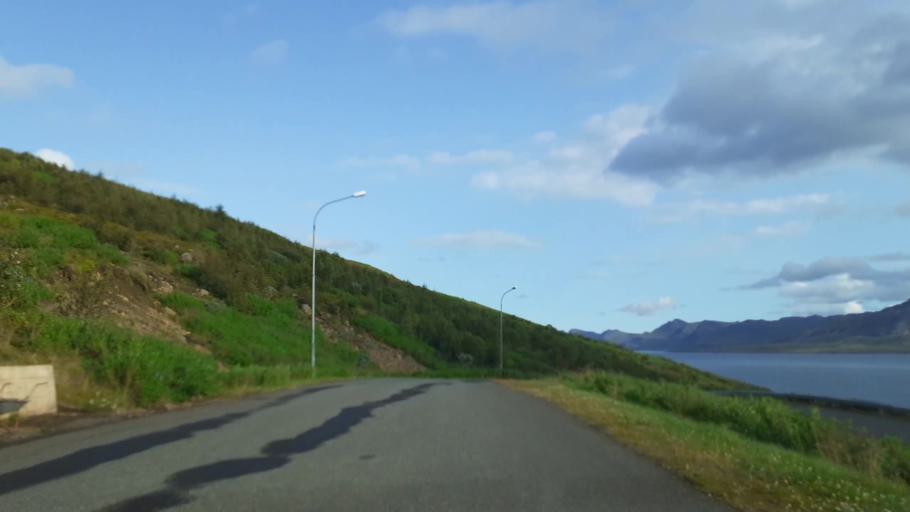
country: IS
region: East
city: Eskifjoerdur
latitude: 65.0644
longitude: -13.9945
